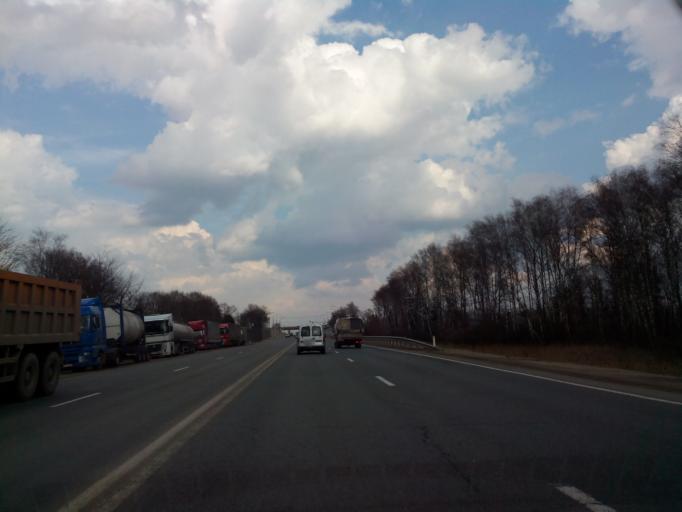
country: RU
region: Moskovskaya
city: Kubinka
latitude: 55.5704
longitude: 36.6901
